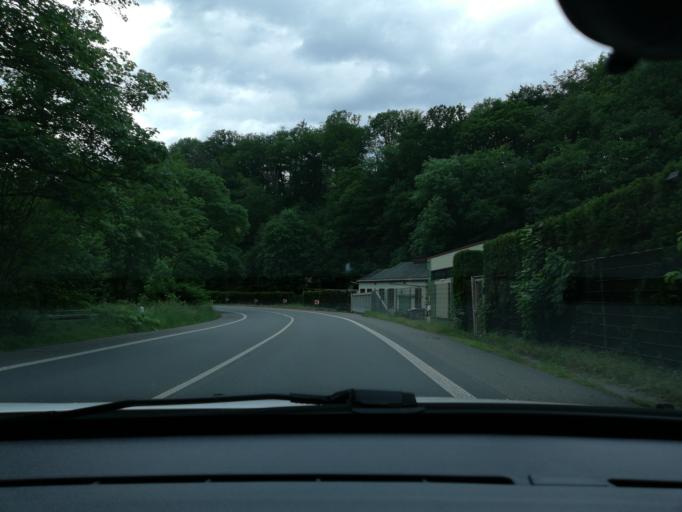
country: DE
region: North Rhine-Westphalia
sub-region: Regierungsbezirk Arnsberg
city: Schalksmuhle
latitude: 51.2988
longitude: 7.5321
